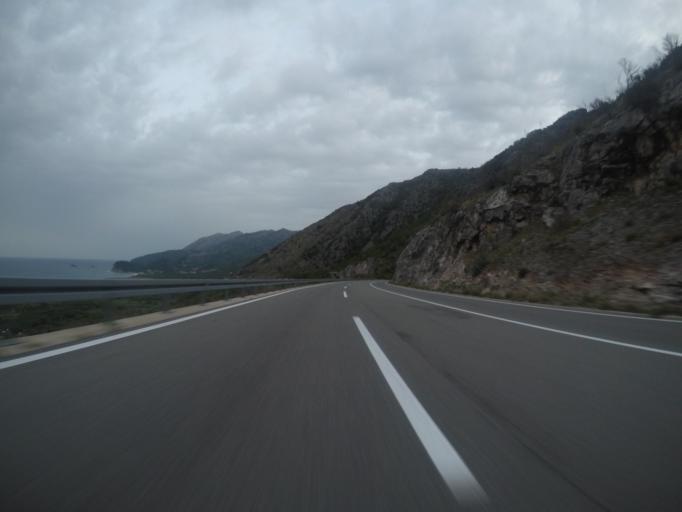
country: ME
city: Petrovac na Moru
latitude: 42.1816
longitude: 18.9947
